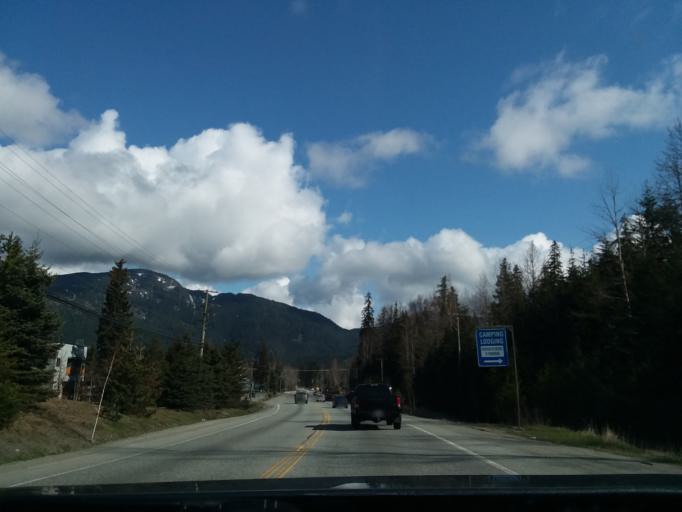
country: CA
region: British Columbia
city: Whistler
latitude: 50.1292
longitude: -122.9540
